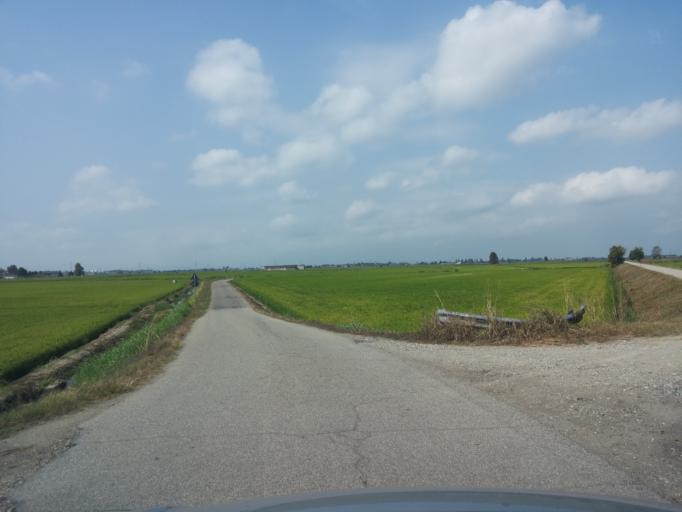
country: IT
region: Lombardy
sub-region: Provincia di Pavia
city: Palestro
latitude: 45.2893
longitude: 8.5119
